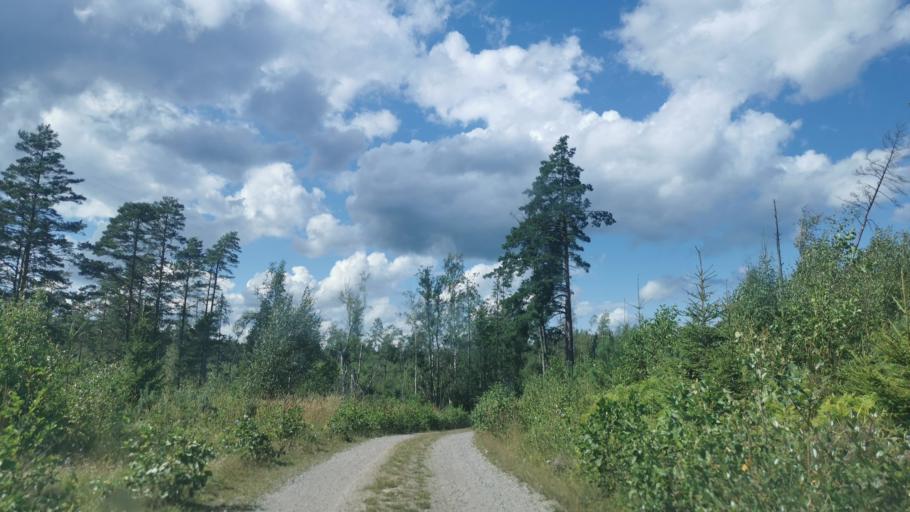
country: SE
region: OEstergoetland
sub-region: Finspangs Kommun
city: Finspang
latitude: 58.7978
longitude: 15.7911
